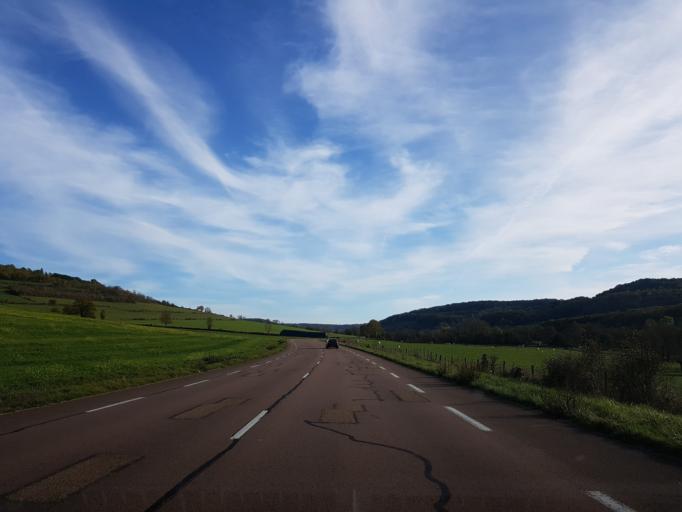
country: FR
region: Bourgogne
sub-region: Departement de la Cote-d'Or
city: Pouilly-en-Auxois
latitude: 47.3327
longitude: 4.5847
